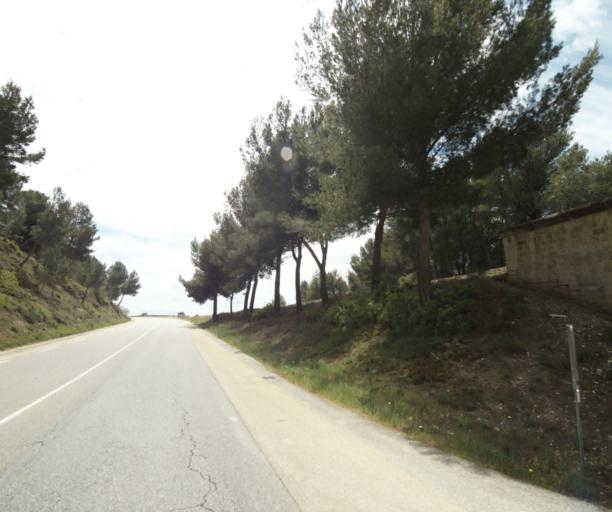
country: FR
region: Provence-Alpes-Cote d'Azur
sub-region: Departement des Bouches-du-Rhone
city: Rognac
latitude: 43.4978
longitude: 5.2313
